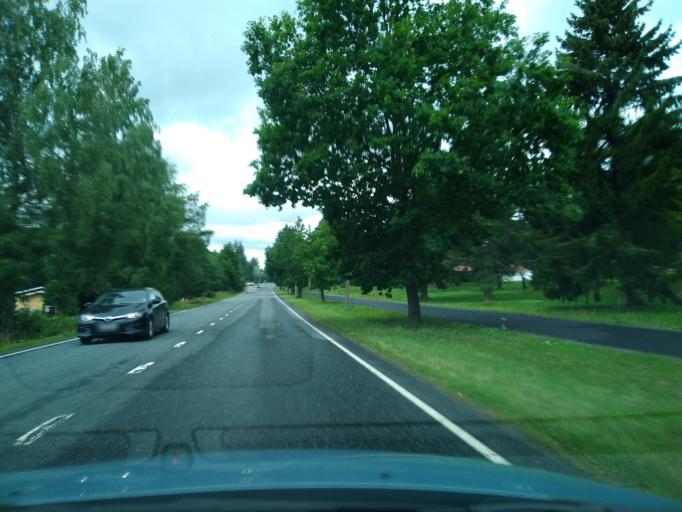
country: FI
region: Haeme
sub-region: Forssa
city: Tammela
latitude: 60.8070
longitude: 23.7663
